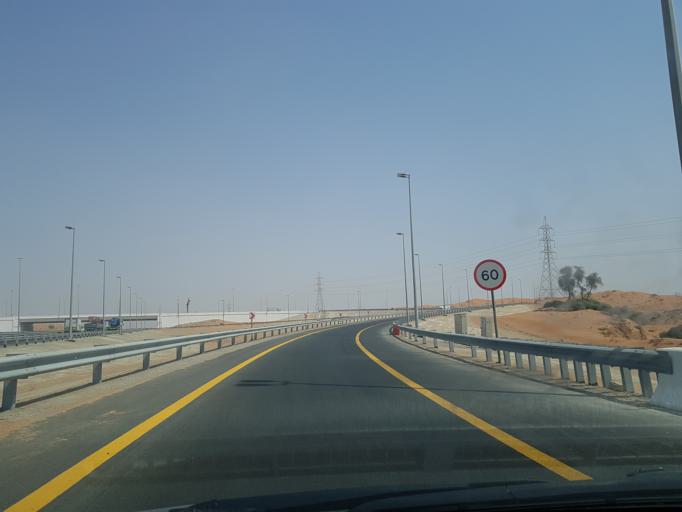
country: AE
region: Ra's al Khaymah
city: Ras al-Khaimah
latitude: 25.6357
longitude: 55.8311
